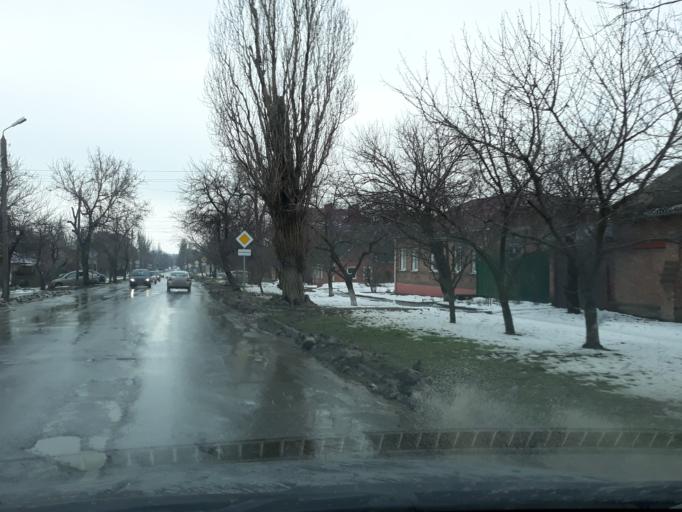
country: RU
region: Rostov
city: Taganrog
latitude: 47.2271
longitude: 38.8985
